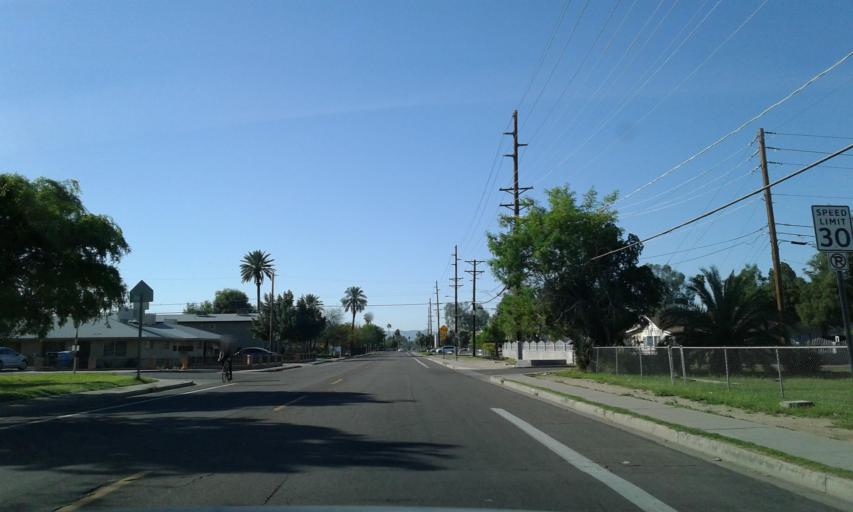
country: US
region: Arizona
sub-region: Maricopa County
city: Phoenix
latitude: 33.5055
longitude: -112.1084
